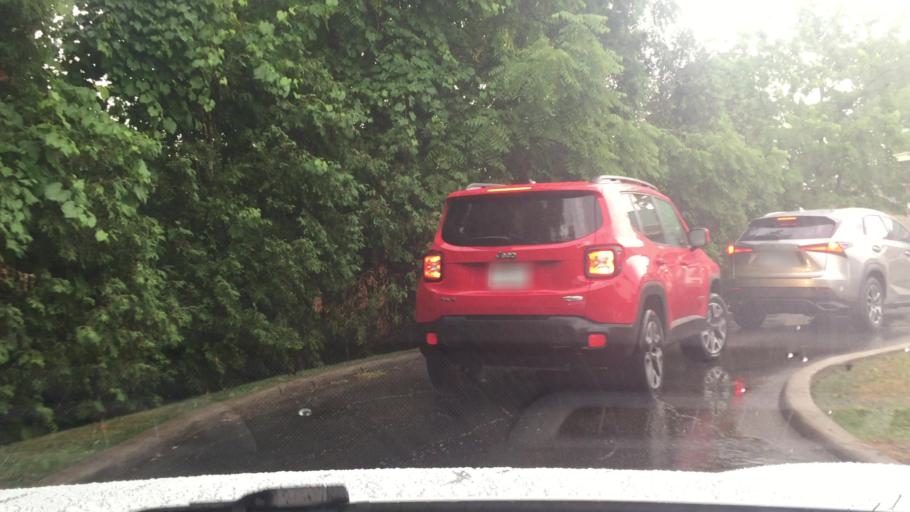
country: CA
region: Ontario
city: Oshawa
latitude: 43.9083
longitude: -78.8020
